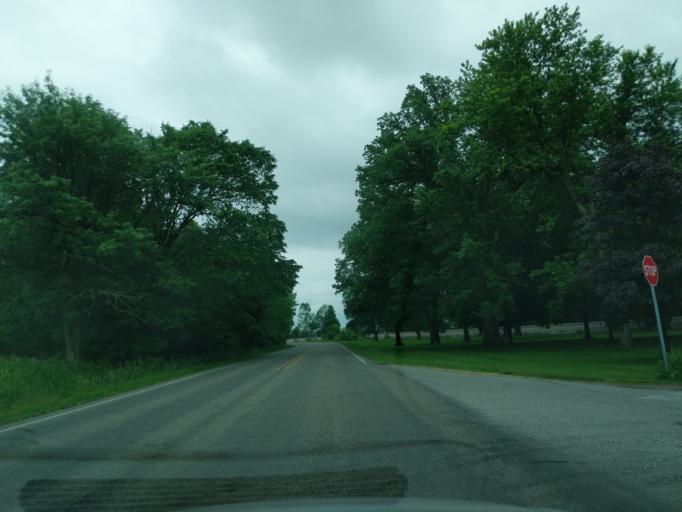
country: US
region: Indiana
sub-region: Tipton County
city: Tipton
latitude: 40.2836
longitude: -85.9420
